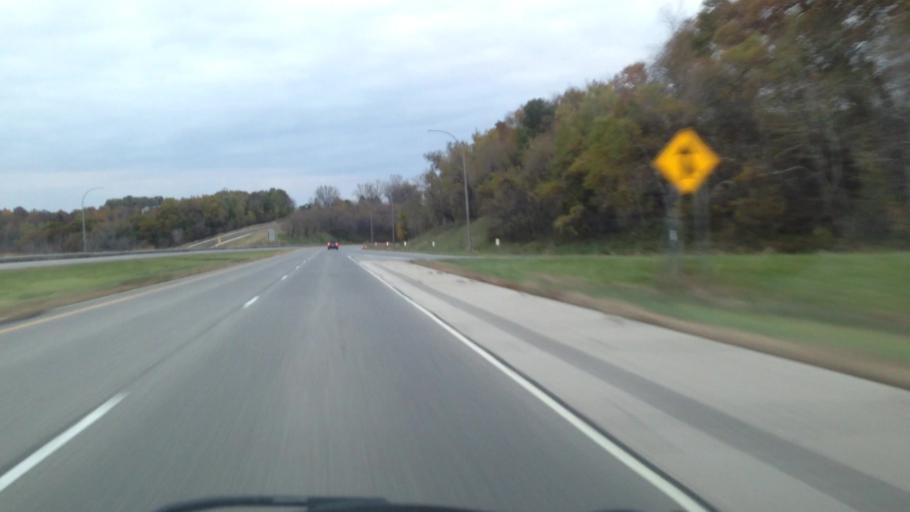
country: US
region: Wisconsin
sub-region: Trempealeau County
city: Trempealeau
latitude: 43.9276
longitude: -91.4383
